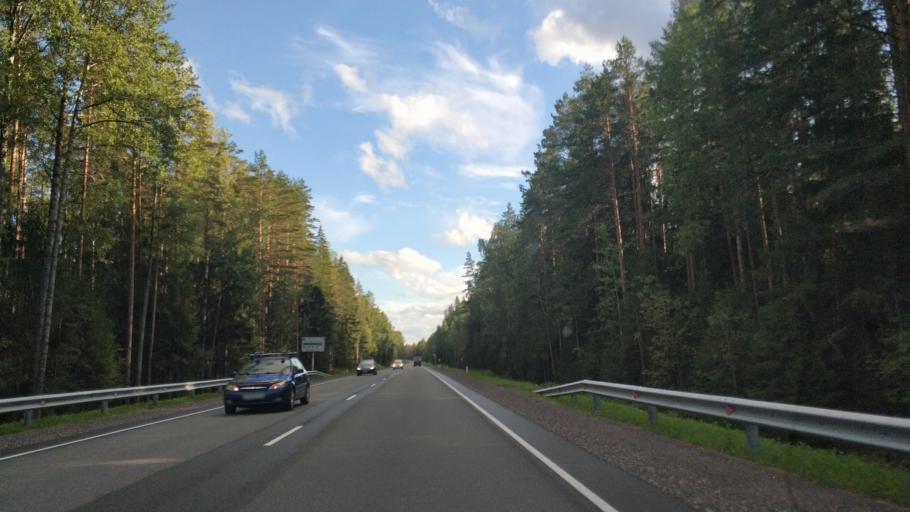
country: RU
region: Leningrad
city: Priozersk
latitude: 60.8986
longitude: 30.1598
